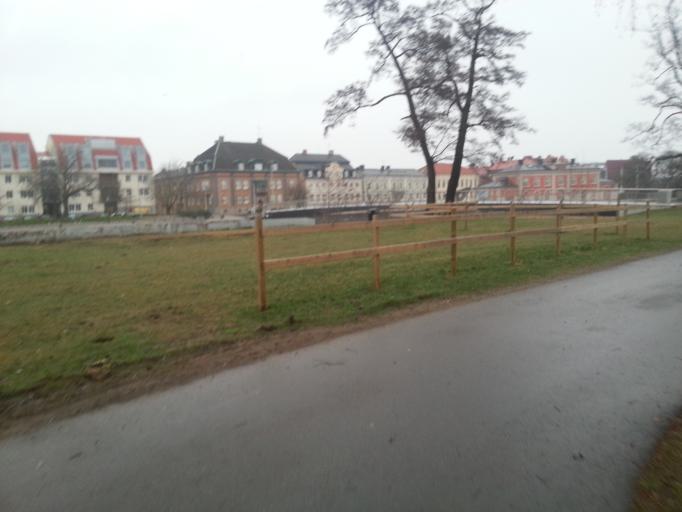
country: SE
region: OEstergoetland
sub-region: Norrkopings Kommun
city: Norrkoping
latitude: 58.5939
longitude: 16.1906
